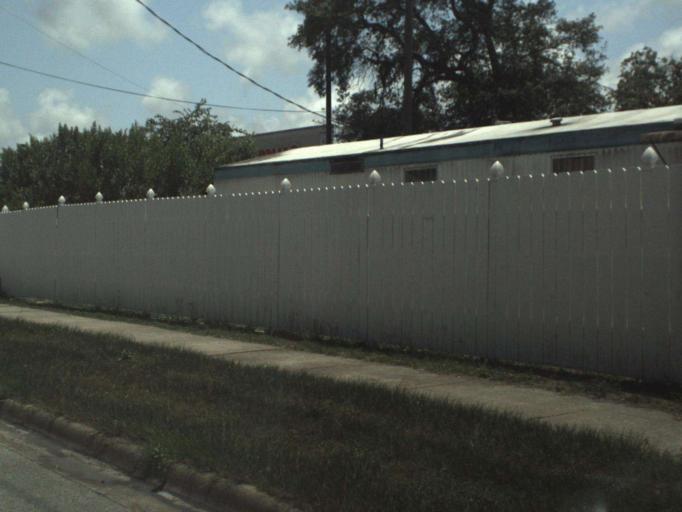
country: US
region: Florida
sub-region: Volusia County
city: Ormond Beach
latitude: 29.2636
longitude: -81.0513
